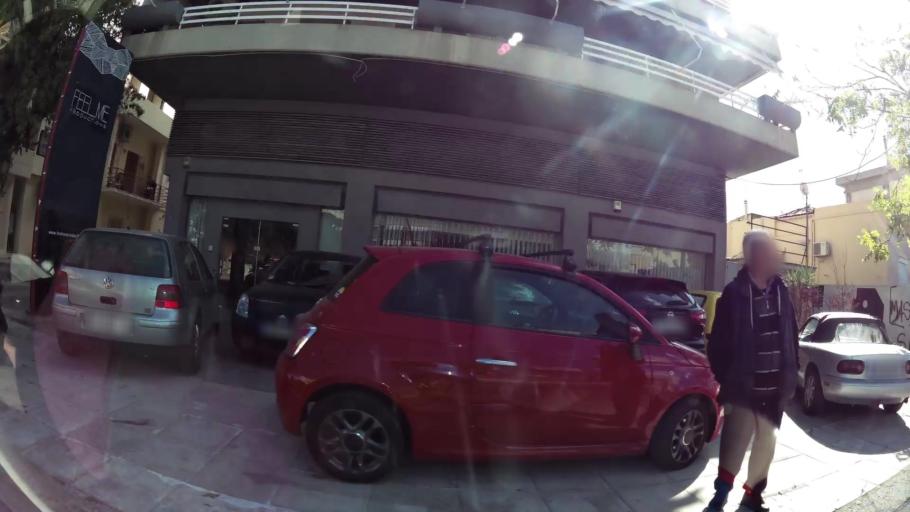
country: GR
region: Attica
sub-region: Nomarchia Athinas
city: Neo Psychiko
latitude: 38.0130
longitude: 23.7905
